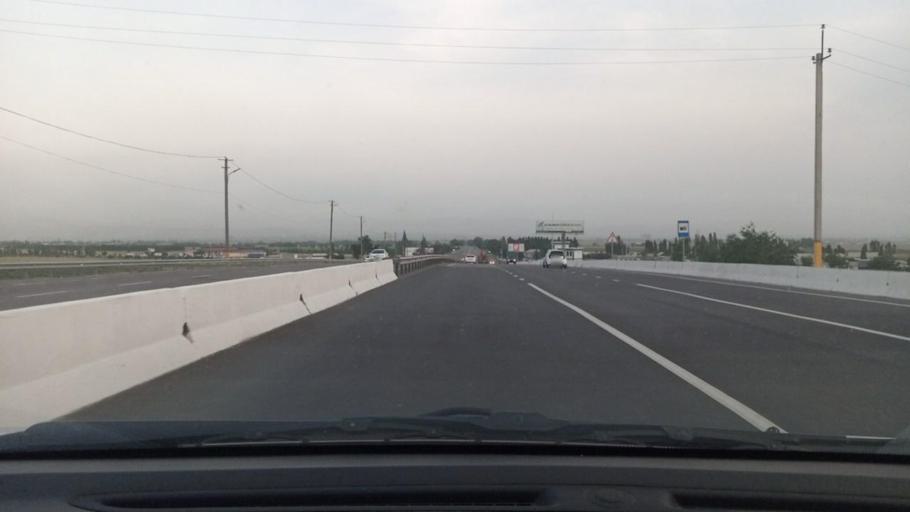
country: UZ
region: Toshkent
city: Ohangaron
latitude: 40.9241
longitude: 69.5971
